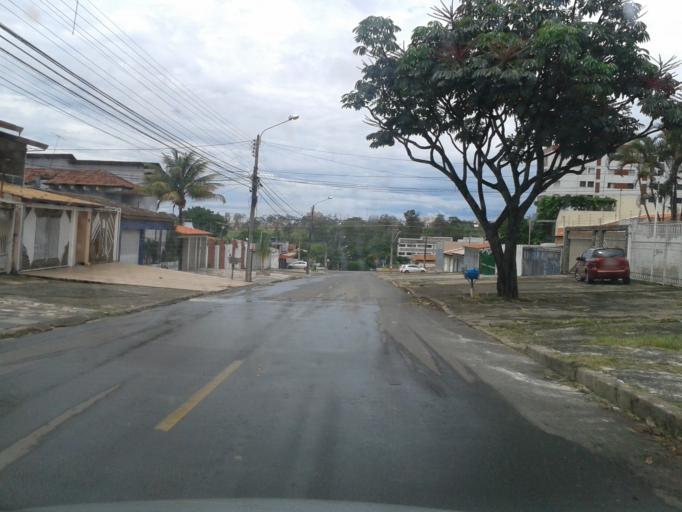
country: BR
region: Federal District
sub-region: Brasilia
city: Brasilia
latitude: -15.8288
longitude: -48.0611
